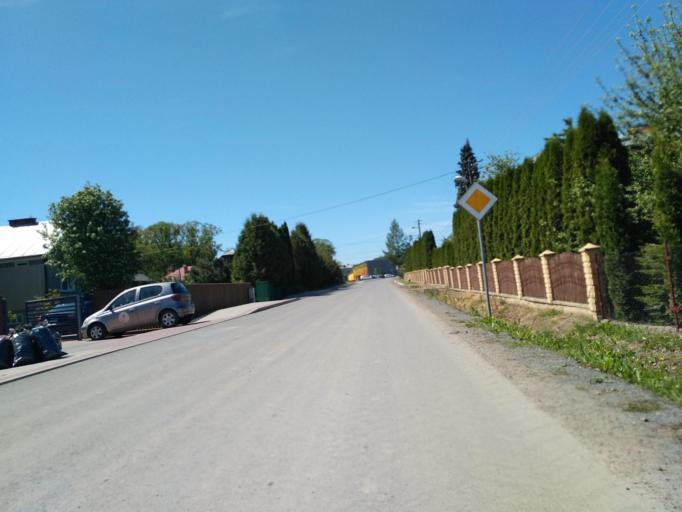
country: PL
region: Subcarpathian Voivodeship
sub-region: Powiat sanocki
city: Besko
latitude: 49.5956
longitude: 21.9658
